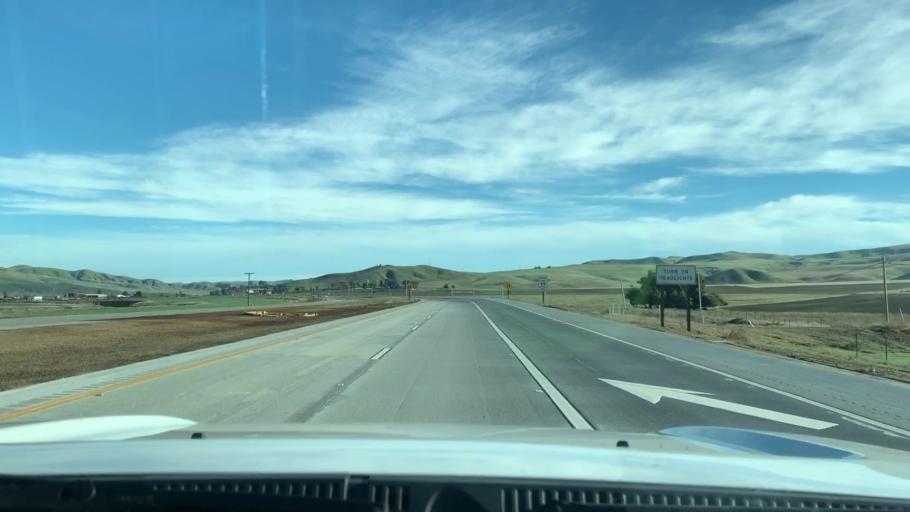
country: US
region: California
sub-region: San Luis Obispo County
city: Shandon
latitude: 35.6759
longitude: -120.3459
